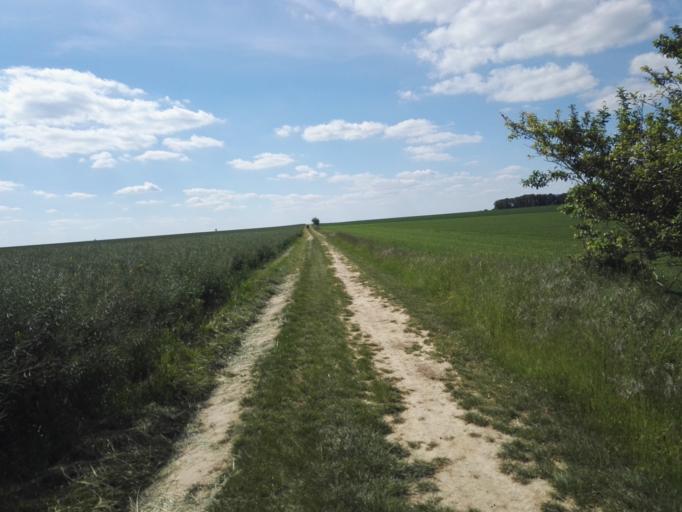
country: FR
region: Haute-Normandie
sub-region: Departement de l'Eure
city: Menilles
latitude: 48.9986
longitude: 1.3411
